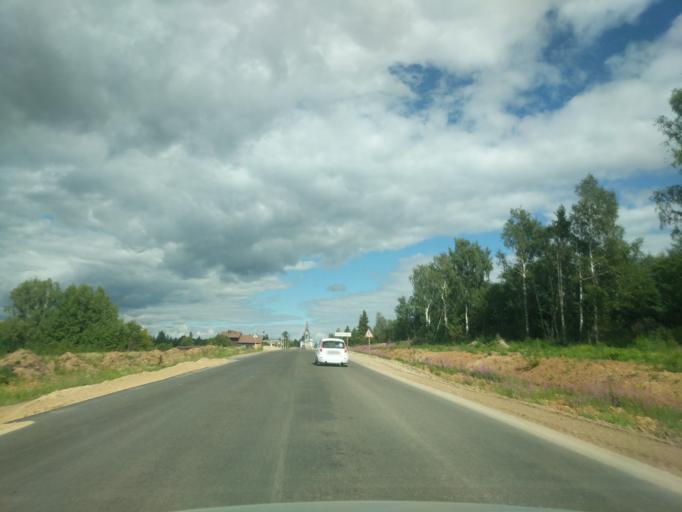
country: RU
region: Kostroma
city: Sudislavl'
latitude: 57.8589
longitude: 41.6119
